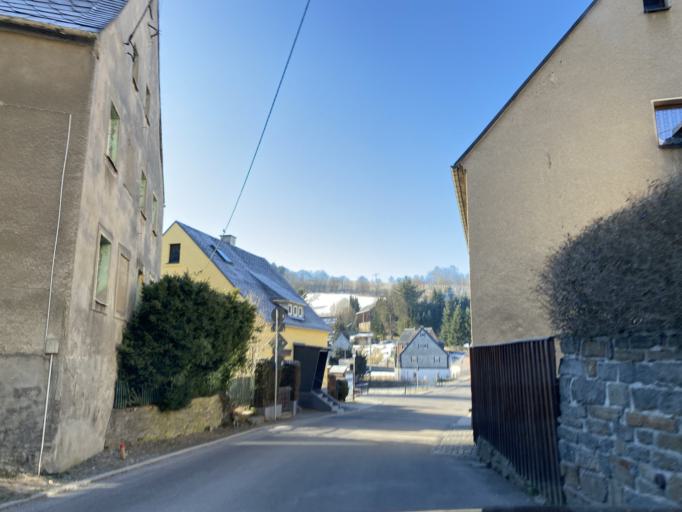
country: DE
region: Saxony
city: Wiesa
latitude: 50.6113
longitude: 13.0204
